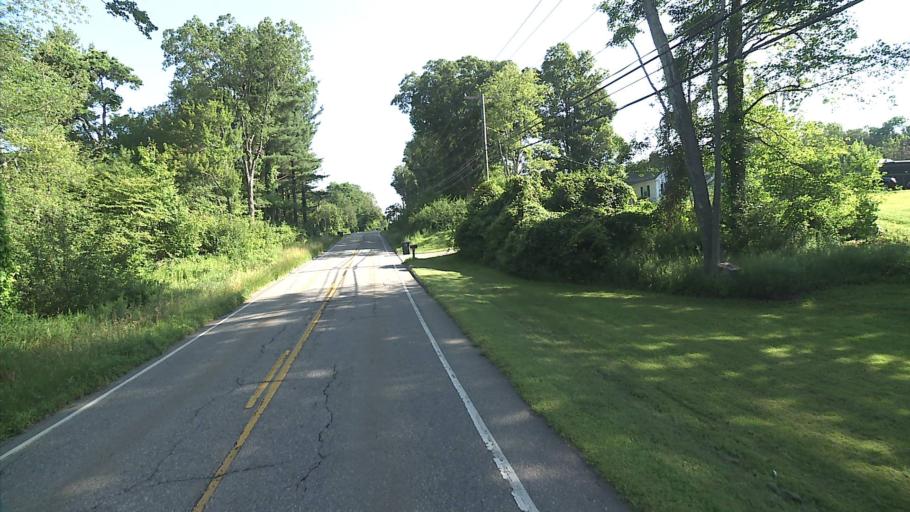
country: US
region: Connecticut
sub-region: Litchfield County
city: Torrington
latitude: 41.8436
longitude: -73.0750
